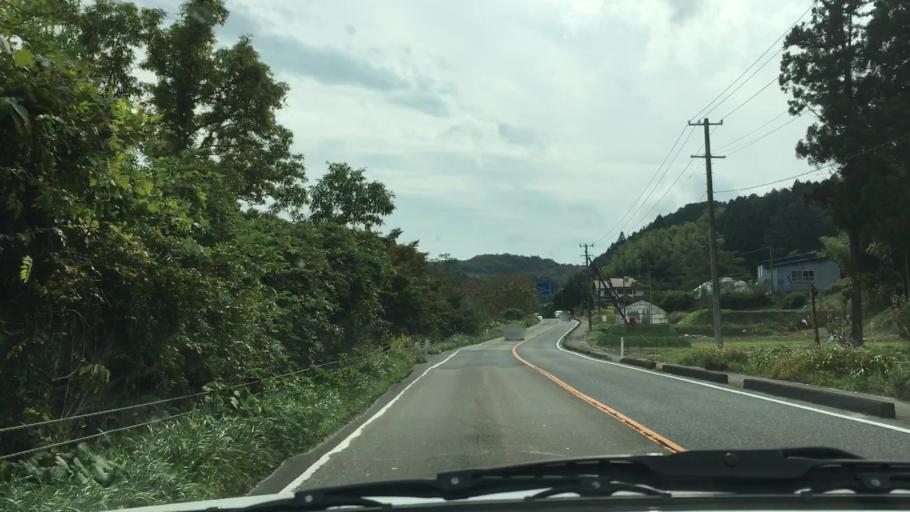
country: JP
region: Miyagi
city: Matsushima
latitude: 38.4242
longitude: 141.0600
